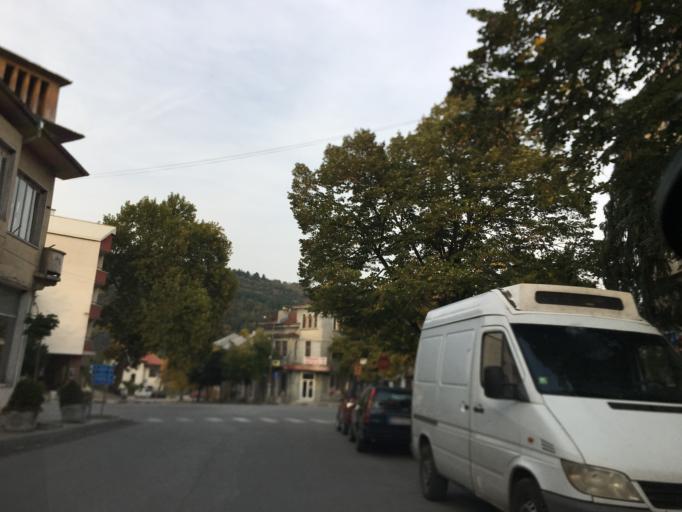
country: BG
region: Pazardzhik
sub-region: Obshtina Belovo
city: Belovo
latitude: 42.2143
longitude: 24.0177
